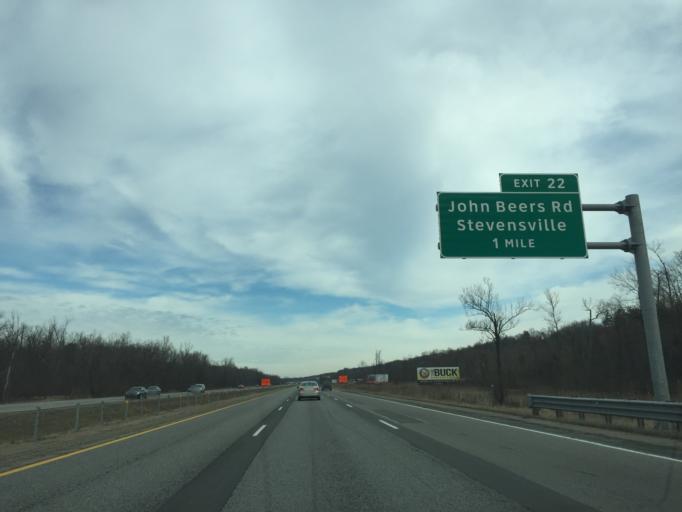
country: US
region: Michigan
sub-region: Berrien County
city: Stevensville
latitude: 41.9920
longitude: -86.5390
